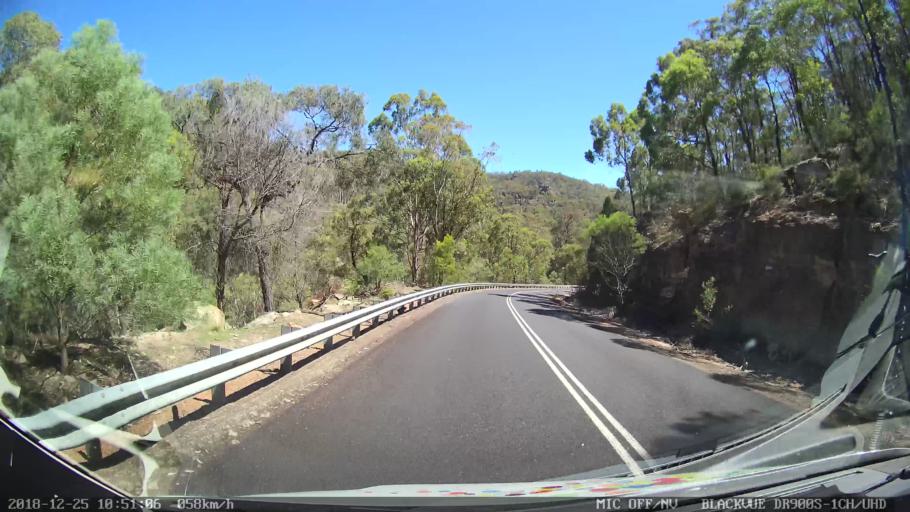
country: AU
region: New South Wales
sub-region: Upper Hunter Shire
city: Merriwa
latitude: -32.4402
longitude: 150.2686
